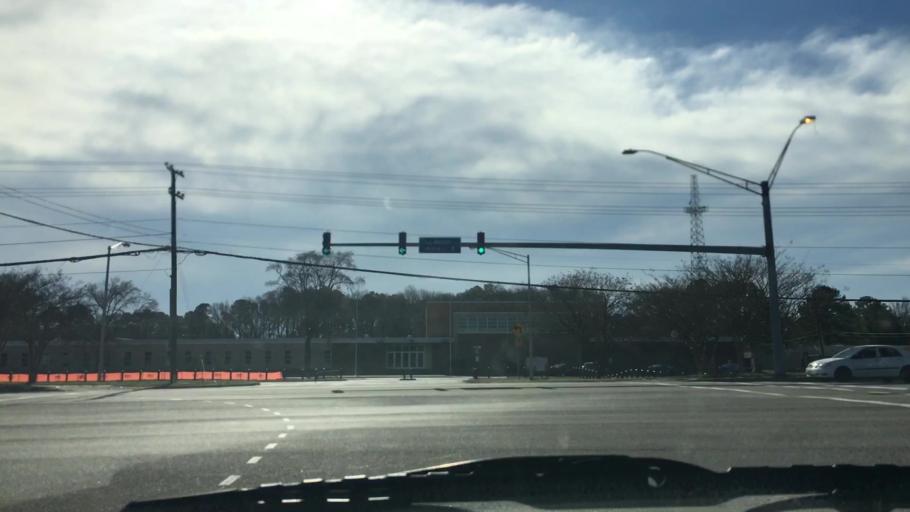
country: US
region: Virginia
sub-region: City of Norfolk
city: Norfolk
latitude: 36.8561
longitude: -76.2323
